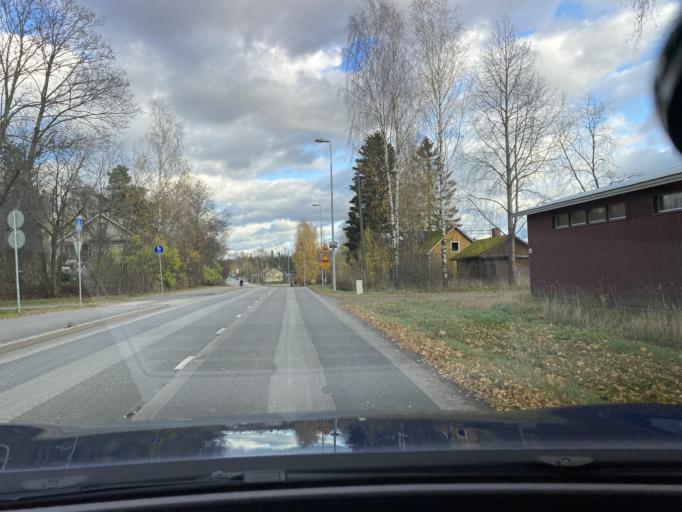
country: FI
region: Paijanne Tavastia
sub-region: Lahti
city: Jaervelae
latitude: 60.8661
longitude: 25.2650
